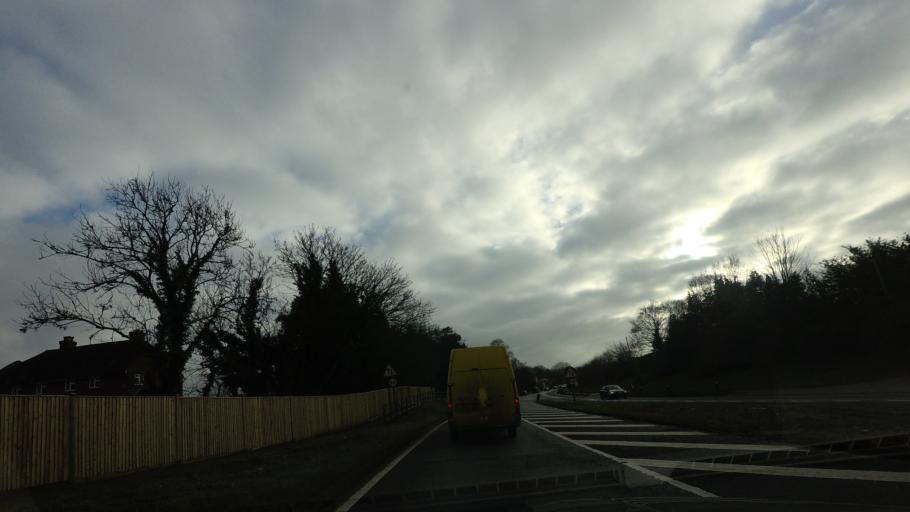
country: GB
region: England
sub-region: Kent
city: Hawkhurst
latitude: 51.0594
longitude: 0.4465
